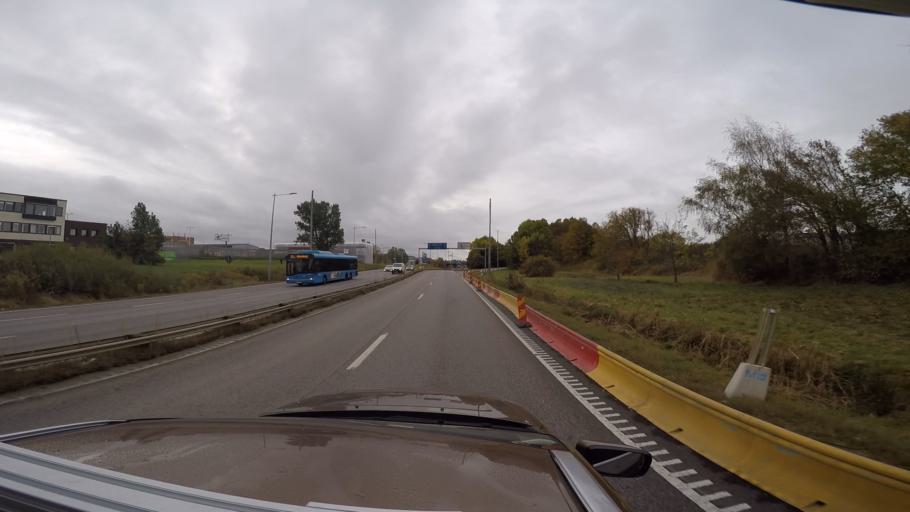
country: SE
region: Vaestra Goetaland
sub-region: Goteborg
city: Majorna
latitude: 57.6515
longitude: 11.9336
